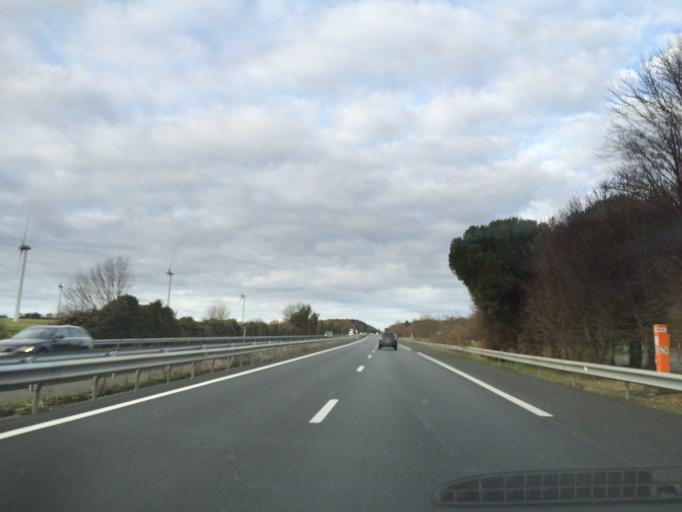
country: FR
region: Poitou-Charentes
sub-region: Departement de la Charente-Maritime
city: Saint-Jean-d'Angely
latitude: 46.0106
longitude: -0.5407
